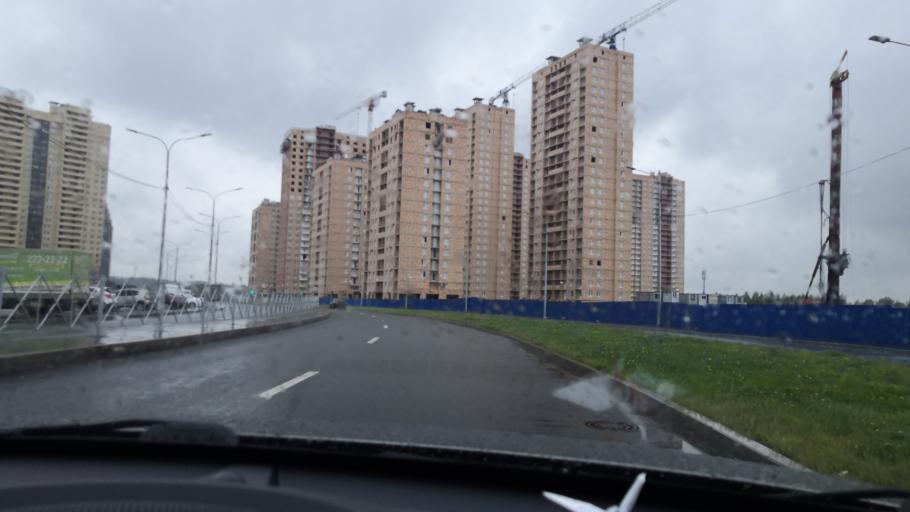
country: RU
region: Leningrad
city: Parnas
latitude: 60.0839
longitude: 30.3507
